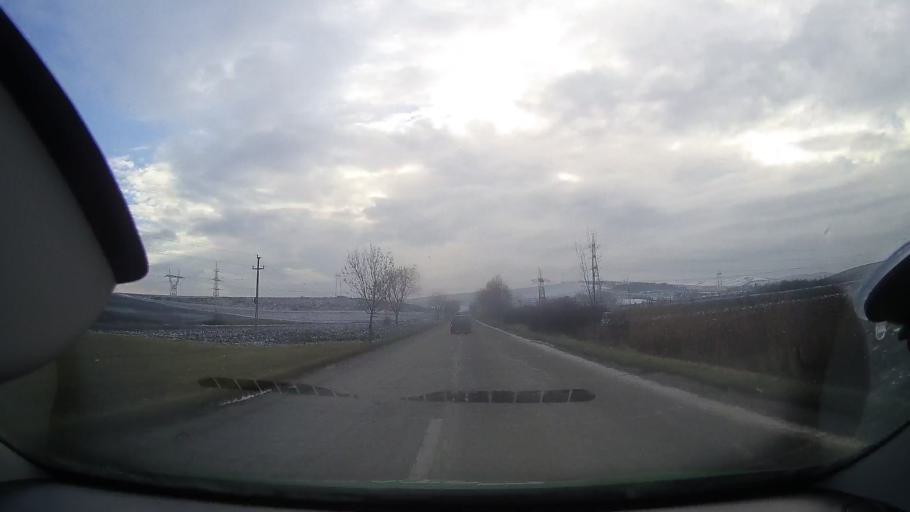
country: RO
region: Mures
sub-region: Comuna Cucerdea
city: Cucerdea
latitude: 46.4244
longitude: 24.2597
